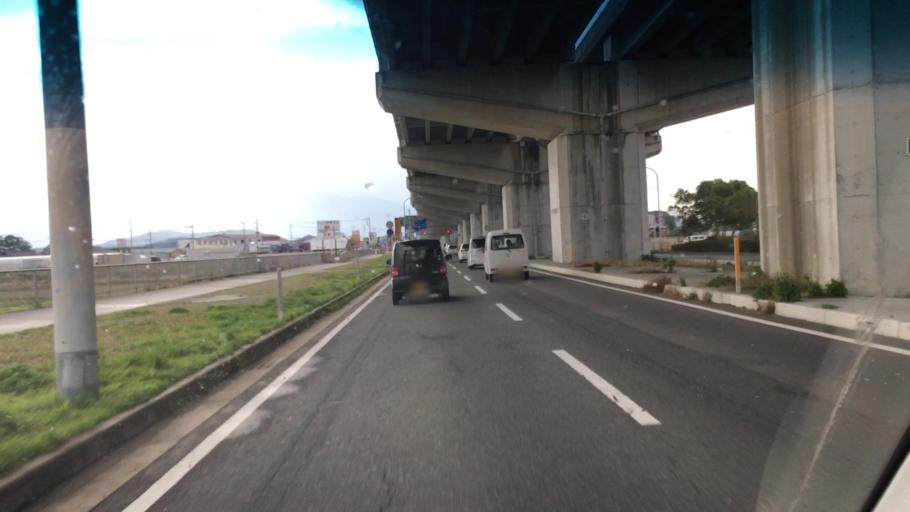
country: JP
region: Fukuoka
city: Maebaru-chuo
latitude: 33.5593
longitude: 130.2309
